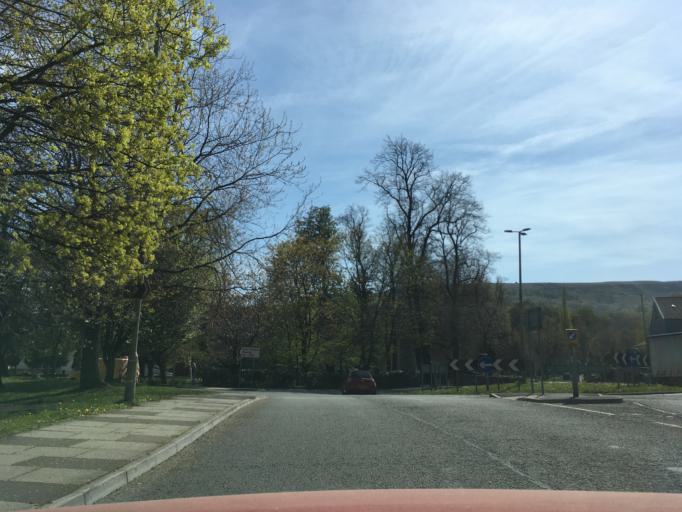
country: GB
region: Wales
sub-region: Rhondda Cynon Taf
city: Aberdare
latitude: 51.7148
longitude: -3.4489
